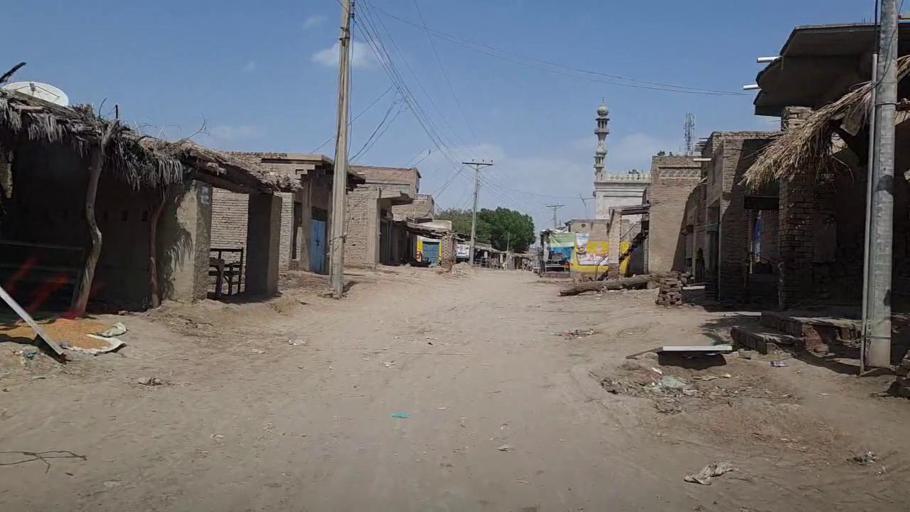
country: PK
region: Sindh
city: Karaundi
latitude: 26.8096
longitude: 68.3923
